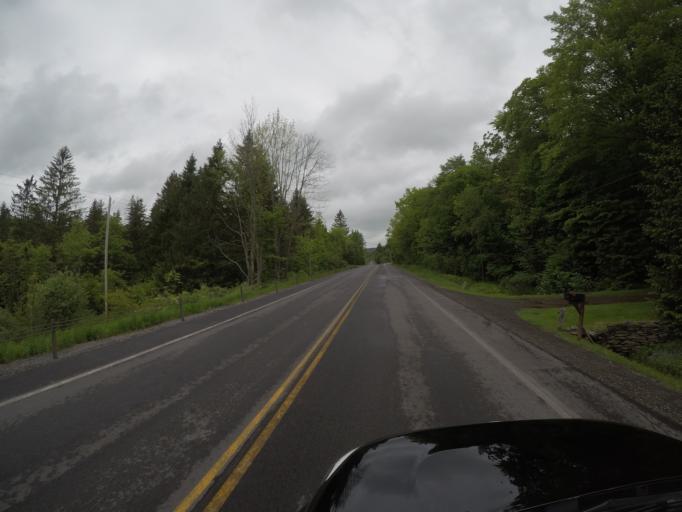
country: US
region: New York
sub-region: Delaware County
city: Delhi
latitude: 42.2179
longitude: -74.7891
